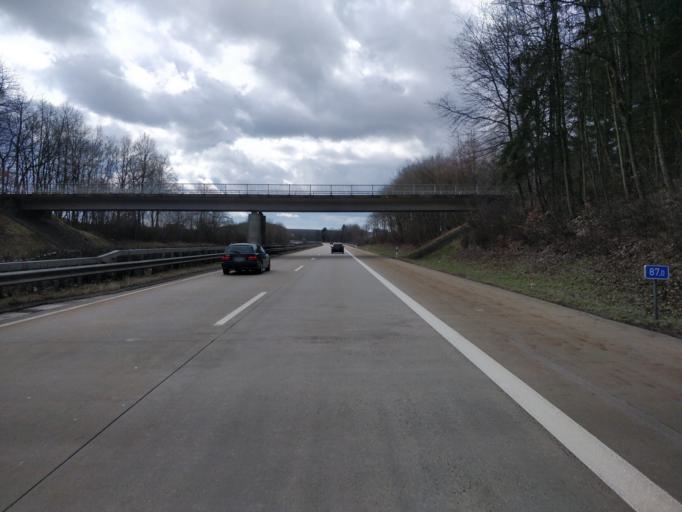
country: DE
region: Rheinland-Pfalz
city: Eckfeld
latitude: 50.1208
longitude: 6.8538
